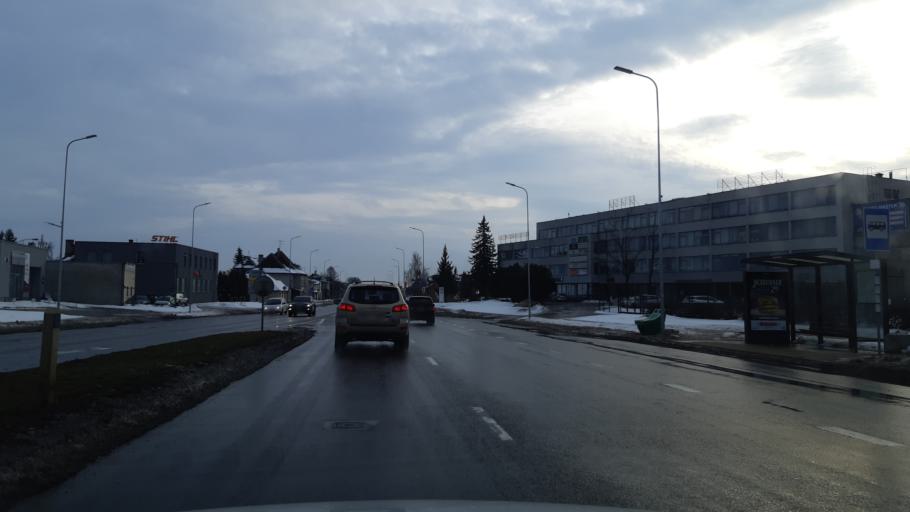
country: LT
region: Kauno apskritis
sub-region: Kaunas
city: Aleksotas
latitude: 54.8746
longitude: 23.8912
